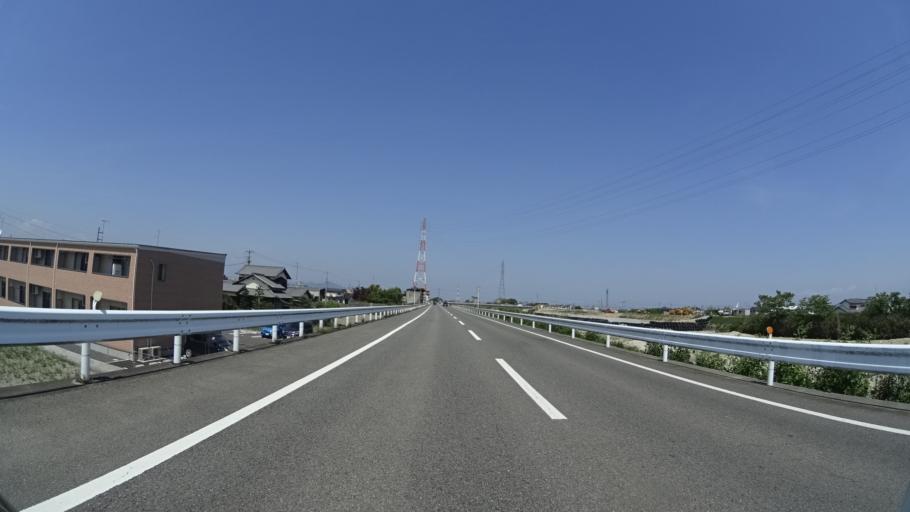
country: JP
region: Ehime
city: Hojo
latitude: 34.0363
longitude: 132.9738
